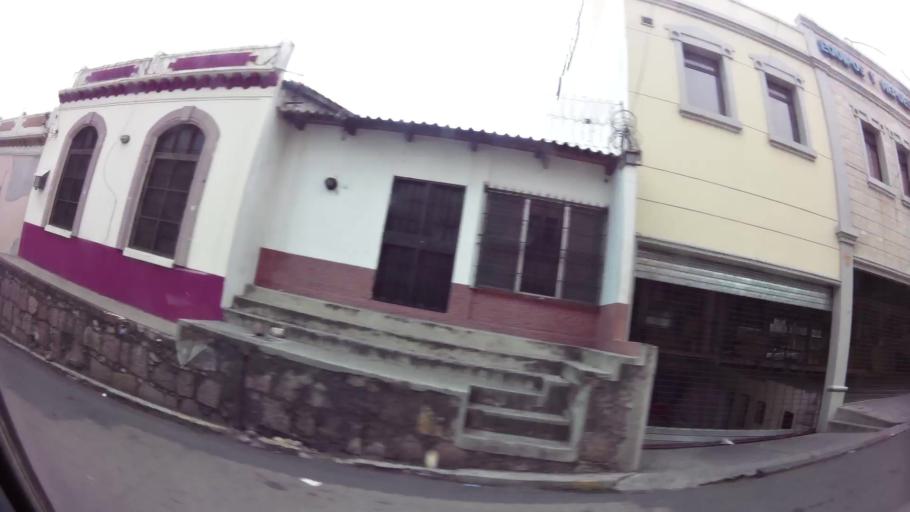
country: HN
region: Francisco Morazan
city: Tegucigalpa
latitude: 14.0938
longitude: -87.2078
